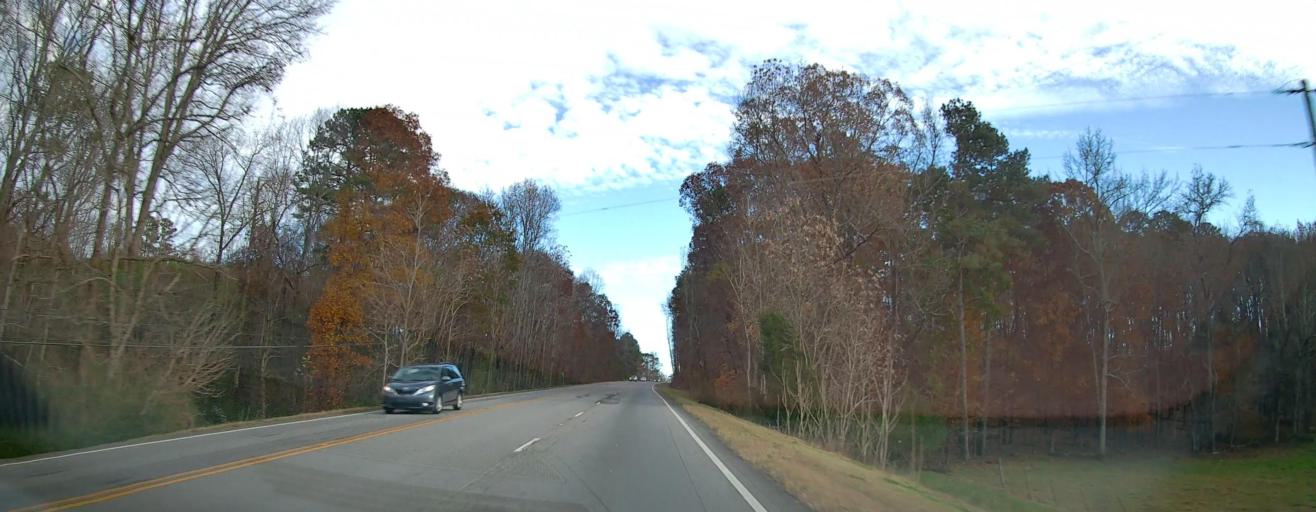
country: US
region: Alabama
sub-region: Marshall County
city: Arab
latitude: 34.3548
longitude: -86.6219
